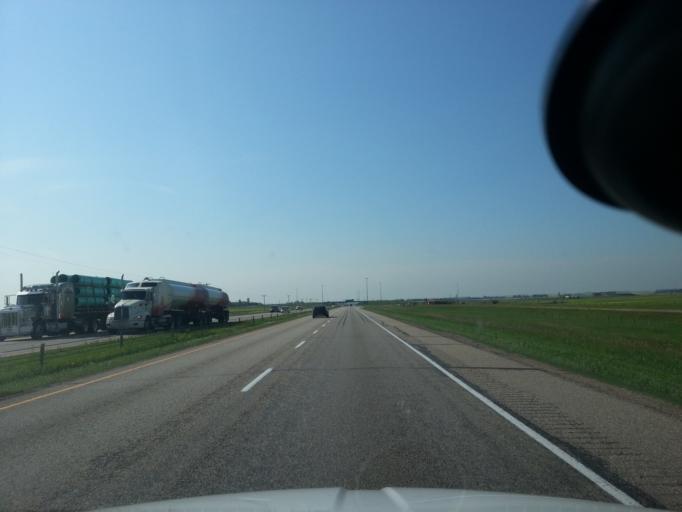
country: CA
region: Alberta
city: Olds
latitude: 51.8030
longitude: -114.0256
